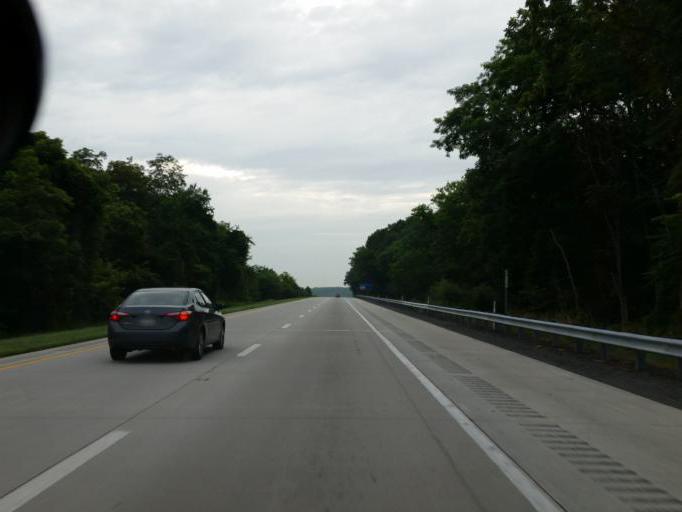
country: US
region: Pennsylvania
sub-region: Lancaster County
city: Elizabethtown
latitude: 40.1913
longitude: -76.6267
